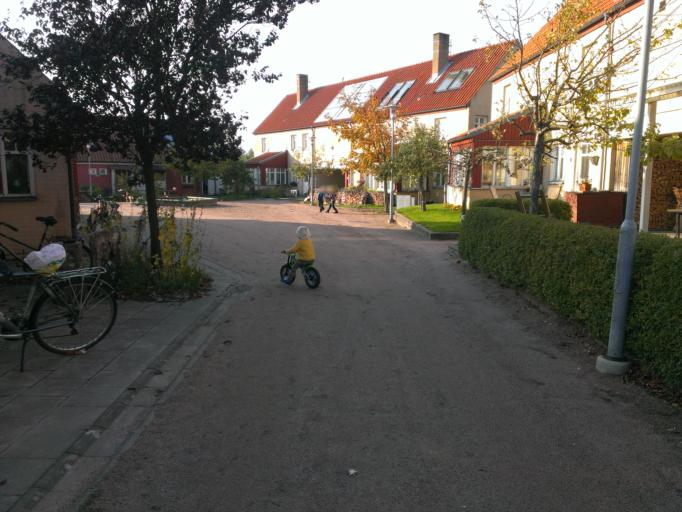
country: SE
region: Skane
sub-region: Malmo
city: Oxie
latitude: 55.5420
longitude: 13.1118
